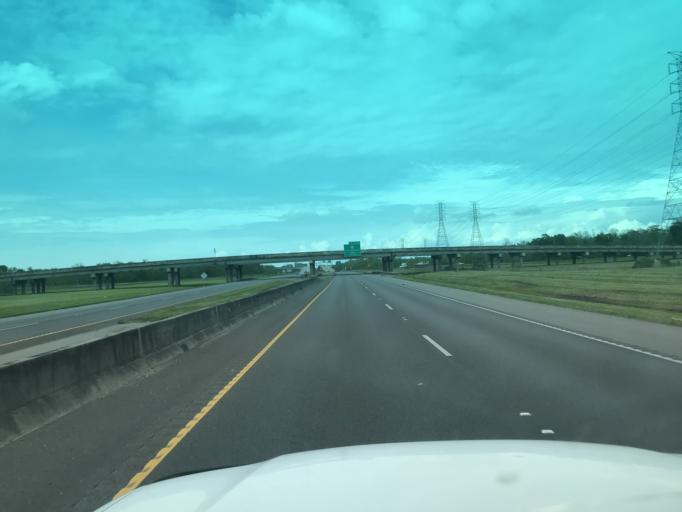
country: US
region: Louisiana
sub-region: Saint Bernard Parish
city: Chalmette
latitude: 30.0161
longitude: -89.9395
